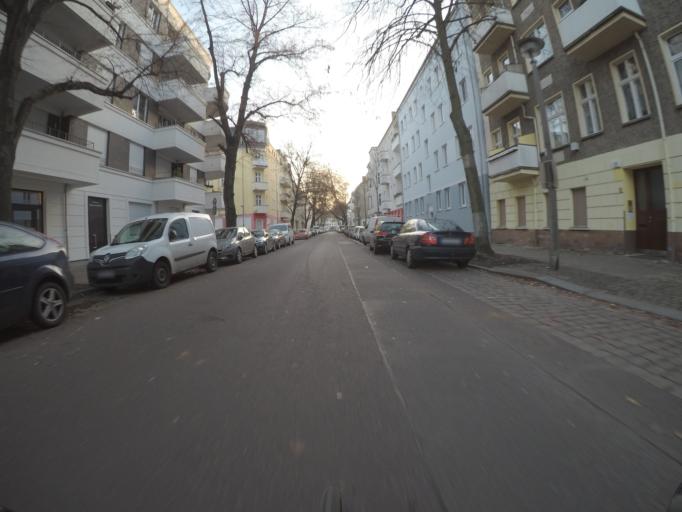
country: DE
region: Berlin
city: Rummelsburg
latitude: 52.5034
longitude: 13.4906
